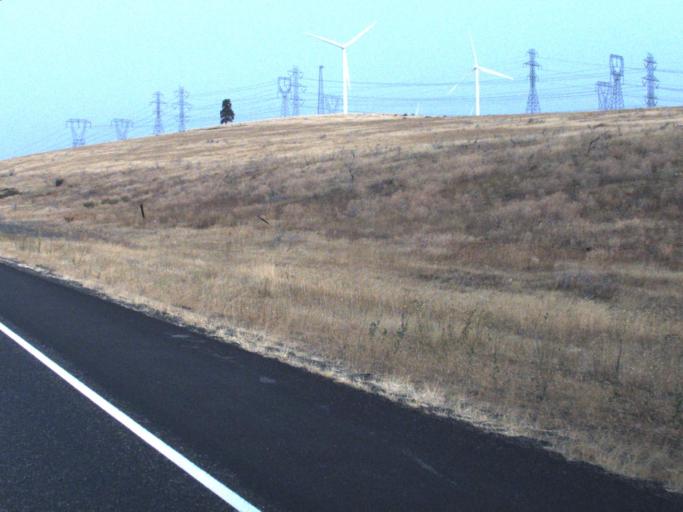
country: US
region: Washington
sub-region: Kittitas County
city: Ellensburg
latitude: 47.1249
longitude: -120.6763
